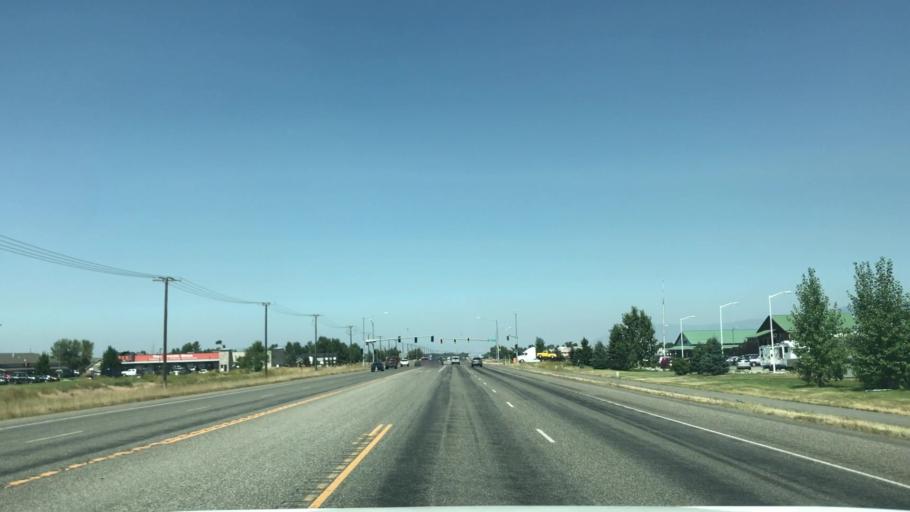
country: US
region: Montana
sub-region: Gallatin County
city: Four Corners
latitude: 45.6770
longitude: -111.1857
